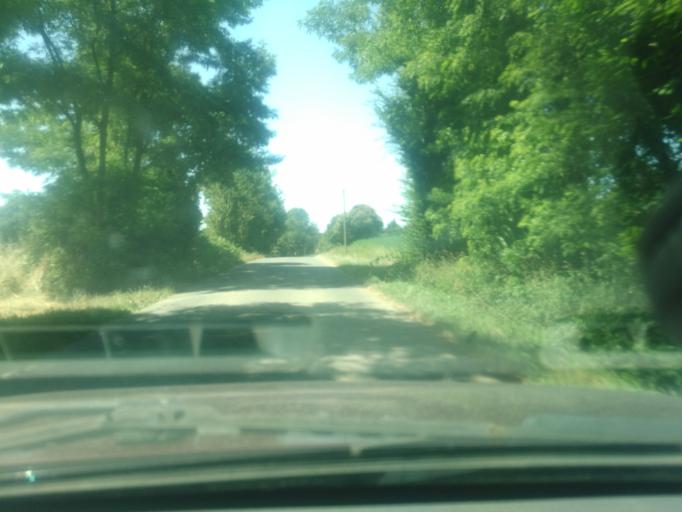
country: FR
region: Pays de la Loire
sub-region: Departement de la Vendee
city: Dompierre-sur-Yon
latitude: 46.7228
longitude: -1.3699
